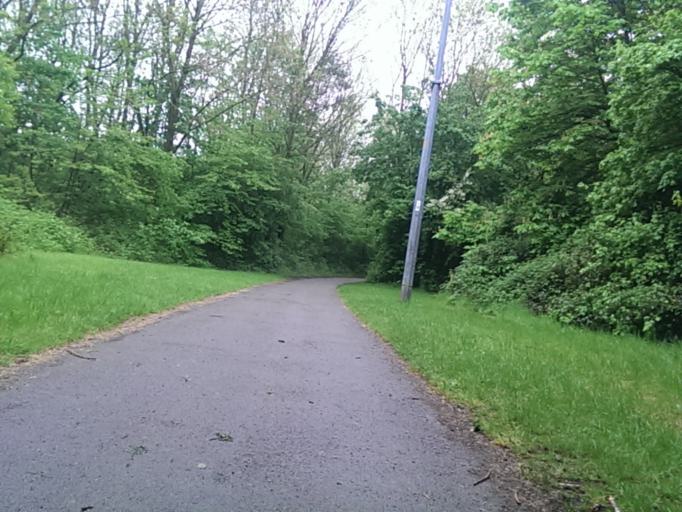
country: GB
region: England
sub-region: Warrington
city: Culcheth
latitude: 53.4239
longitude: -2.5154
